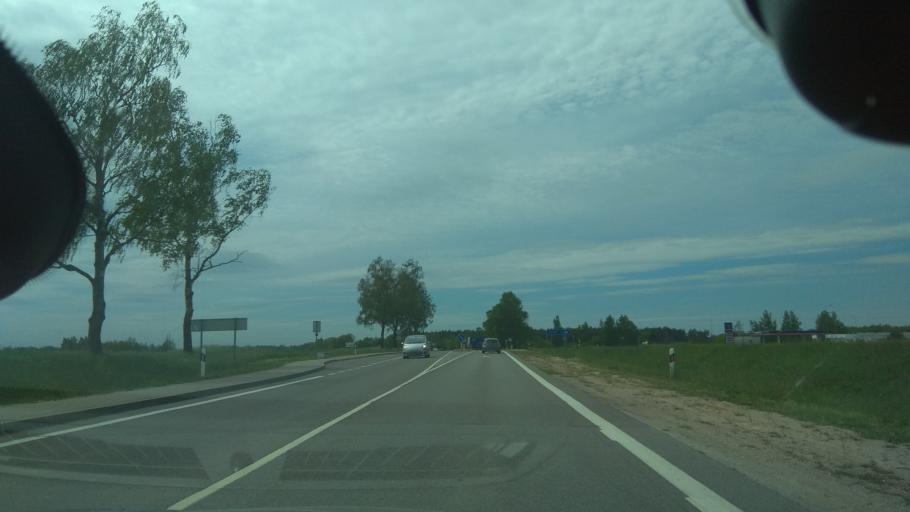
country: LT
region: Kauno apskritis
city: Jonava
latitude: 55.0991
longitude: 24.3206
